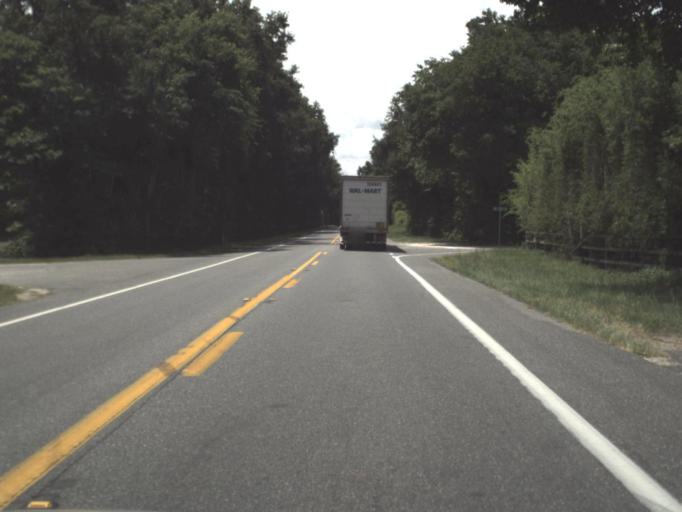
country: US
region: Florida
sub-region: Alachua County
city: Archer
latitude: 29.5860
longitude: -82.5562
